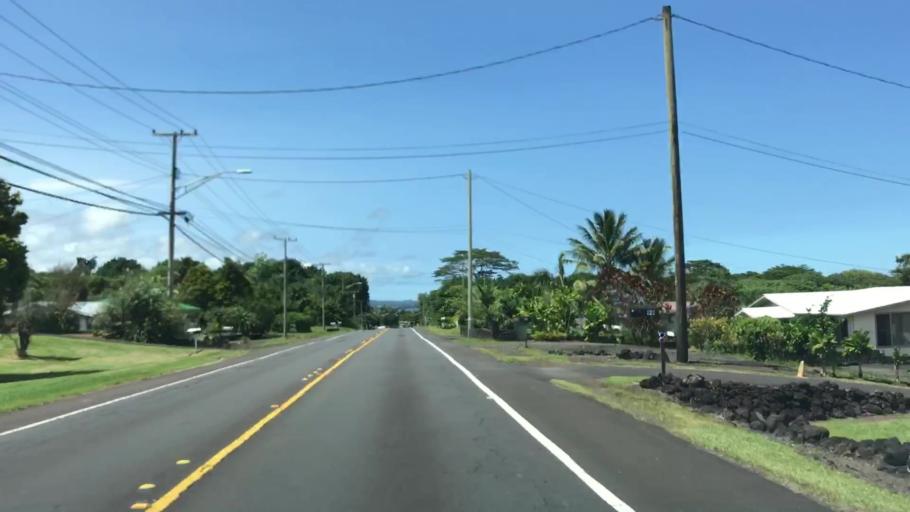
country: US
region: Hawaii
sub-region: Hawaii County
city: Hilo
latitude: 19.6911
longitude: -155.0811
